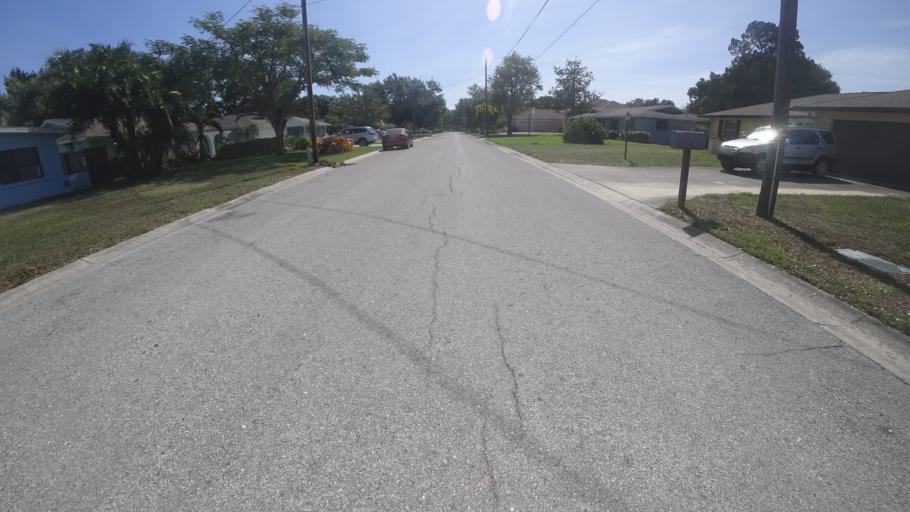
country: US
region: Florida
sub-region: Manatee County
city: West Bradenton
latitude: 27.5020
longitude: -82.6185
